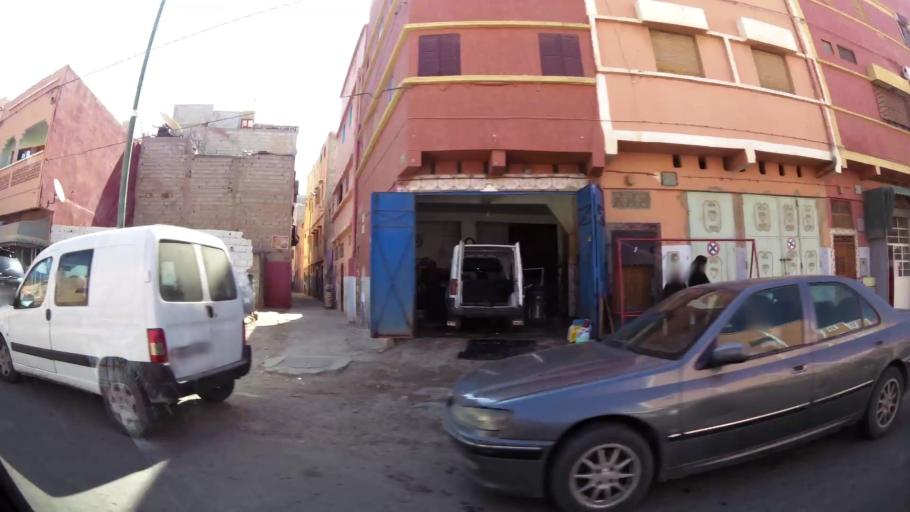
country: MA
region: Souss-Massa-Draa
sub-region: Inezgane-Ait Mellou
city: Inezgane
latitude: 30.3463
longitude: -9.5085
